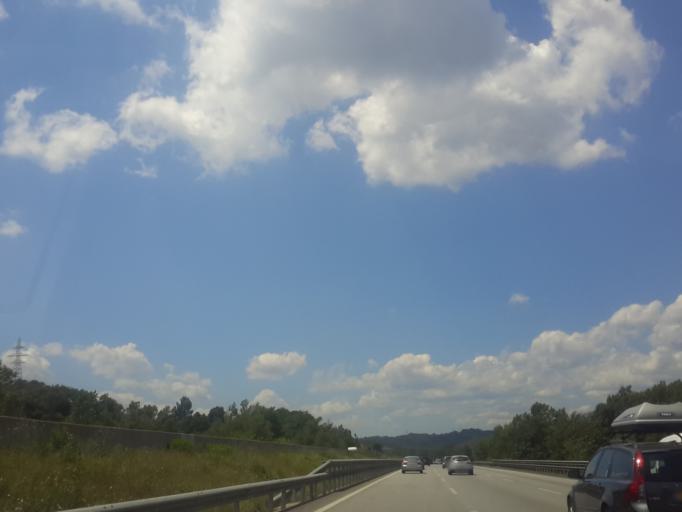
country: ES
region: Catalonia
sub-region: Provincia de Girona
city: Breda
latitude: 41.7137
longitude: 2.5502
